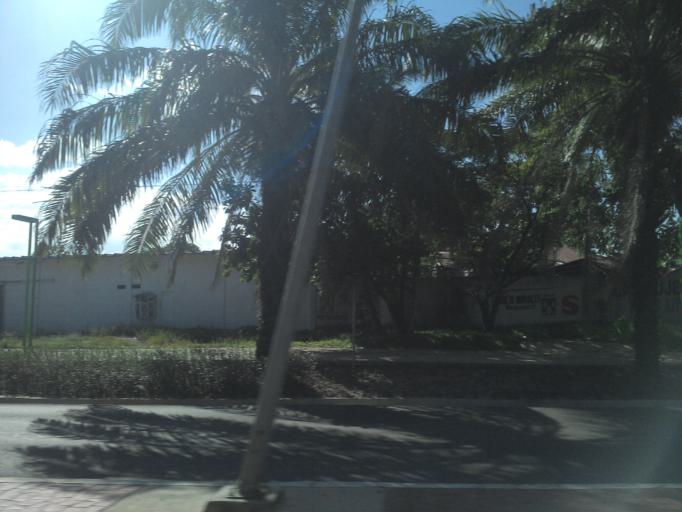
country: MX
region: Chiapas
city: Palenque
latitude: 17.5240
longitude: -91.9925
